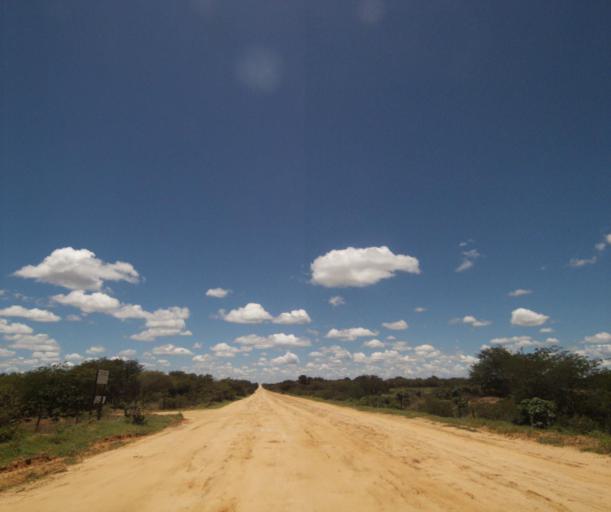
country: BR
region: Bahia
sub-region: Carinhanha
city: Carinhanha
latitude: -14.2794
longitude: -43.7952
